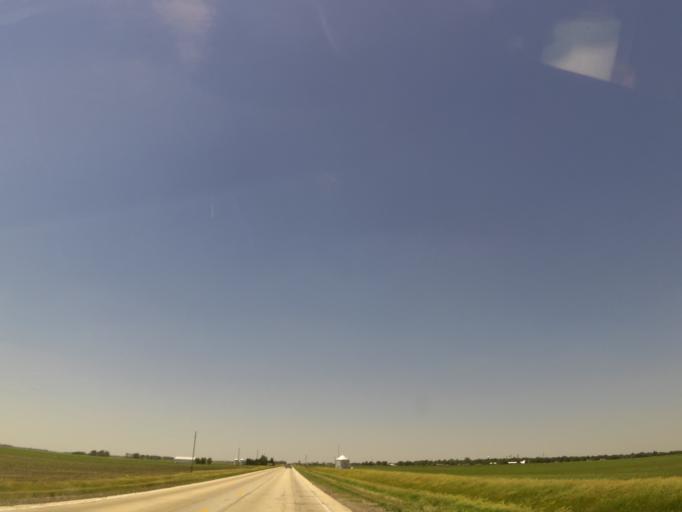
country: US
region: Illinois
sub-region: Livingston County
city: Chatsworth
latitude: 40.7484
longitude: -88.1632
